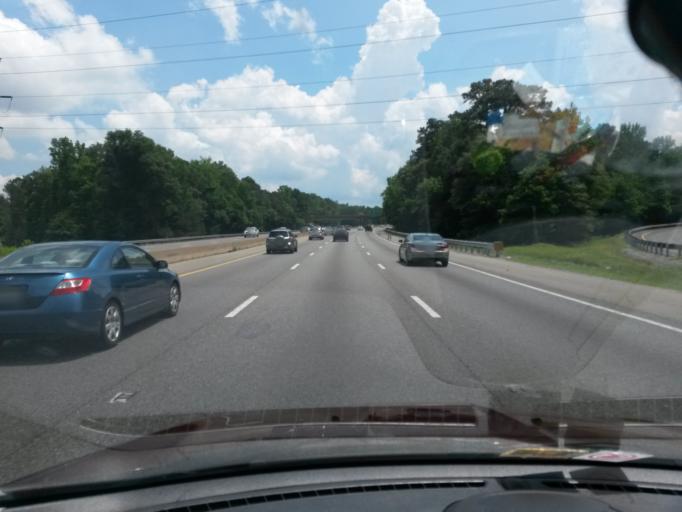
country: US
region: Virginia
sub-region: Chesterfield County
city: Chester
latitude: 37.3799
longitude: -77.4113
